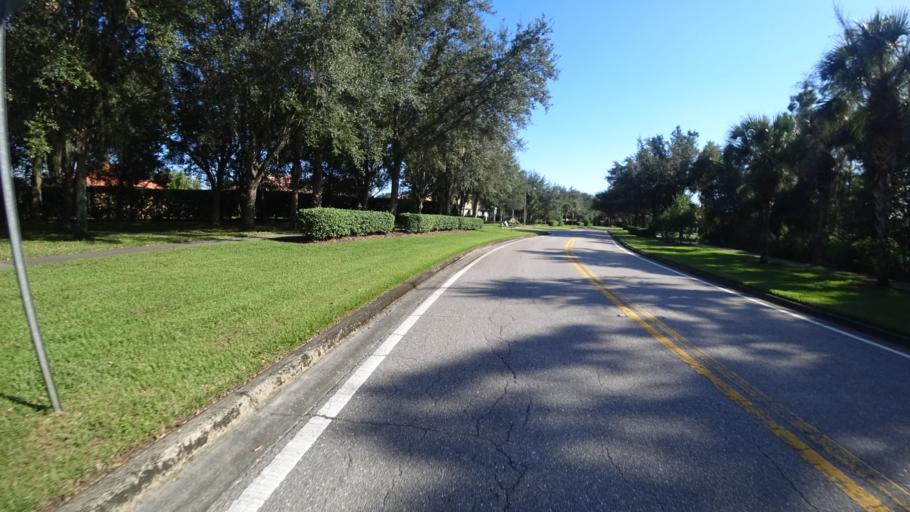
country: US
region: Florida
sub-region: Sarasota County
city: Desoto Lakes
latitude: 27.4221
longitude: -82.4650
